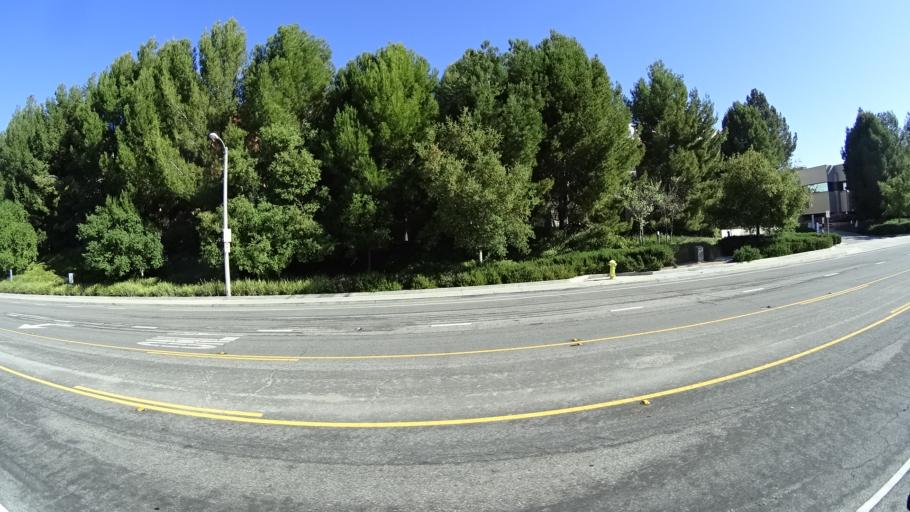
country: US
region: California
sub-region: Ventura County
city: Casa Conejo
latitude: 34.1869
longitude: -118.9237
